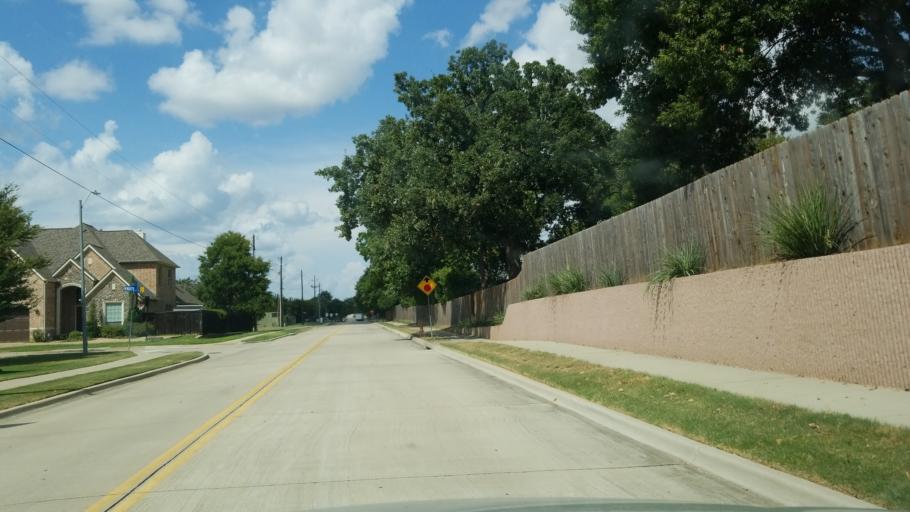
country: US
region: Texas
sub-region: Tarrant County
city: Euless
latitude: 32.8753
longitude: -97.0909
